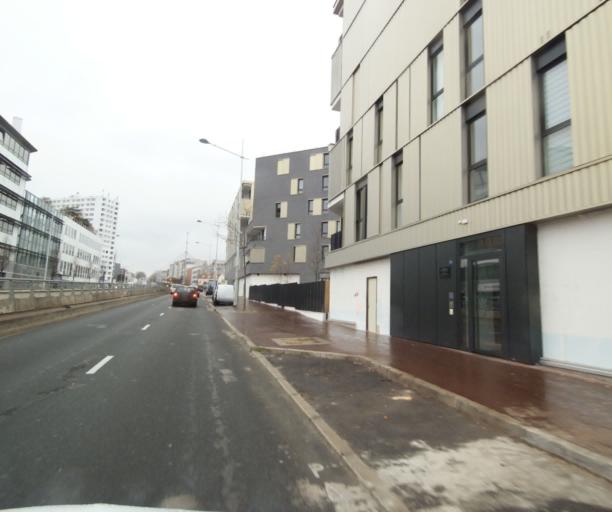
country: FR
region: Ile-de-France
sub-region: Departement des Hauts-de-Seine
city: Nanterre
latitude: 48.8874
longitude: 2.1983
